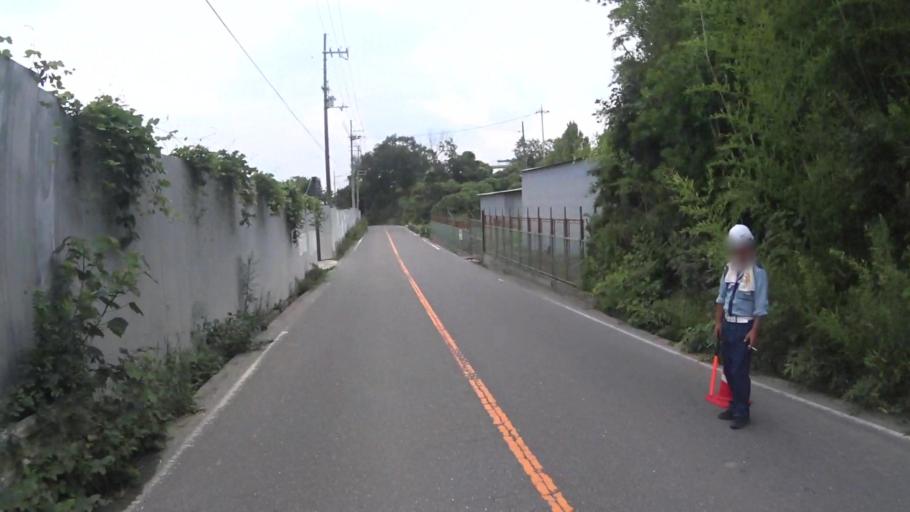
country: JP
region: Nara
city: Nara-shi
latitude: 34.7284
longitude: 135.7917
